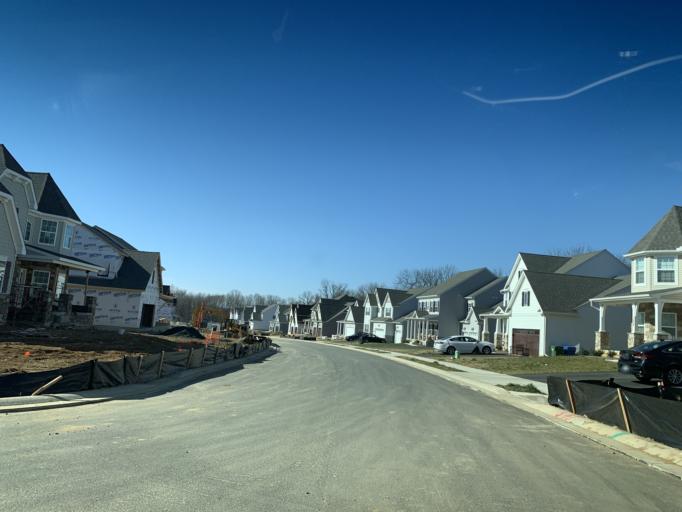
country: US
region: Maryland
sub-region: Harford County
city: South Bel Air
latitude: 39.5563
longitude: -76.3182
